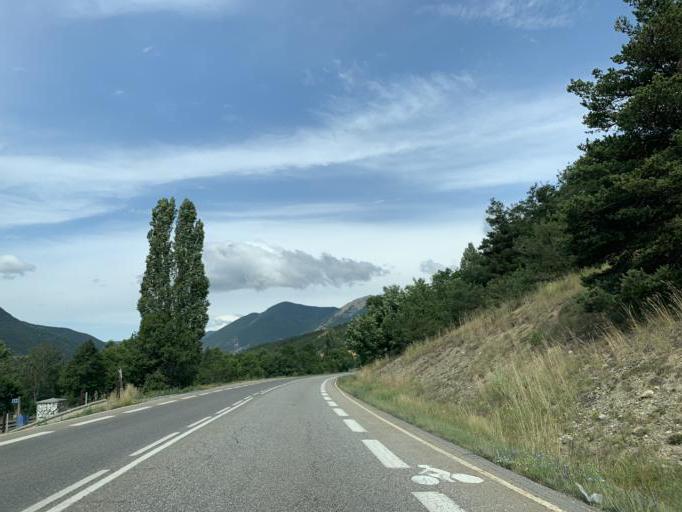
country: FR
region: Provence-Alpes-Cote d'Azur
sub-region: Departement des Hautes-Alpes
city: La Roche-des-Arnauds
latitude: 44.5467
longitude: 5.9848
